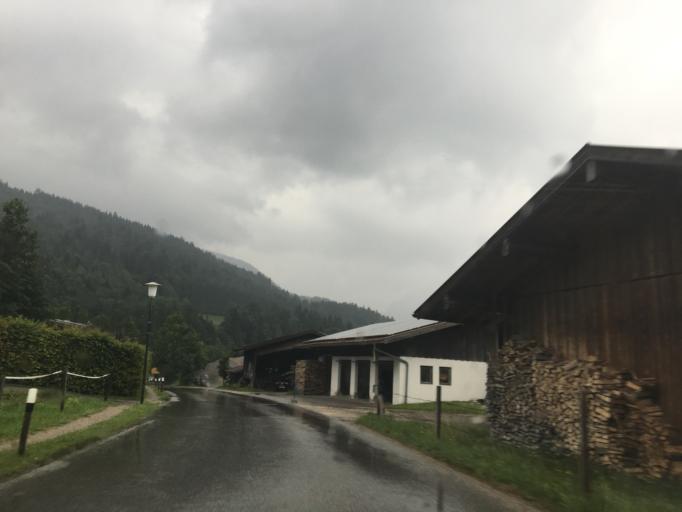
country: DE
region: Bavaria
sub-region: Upper Bavaria
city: Reit im Winkl
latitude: 47.6725
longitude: 12.4889
